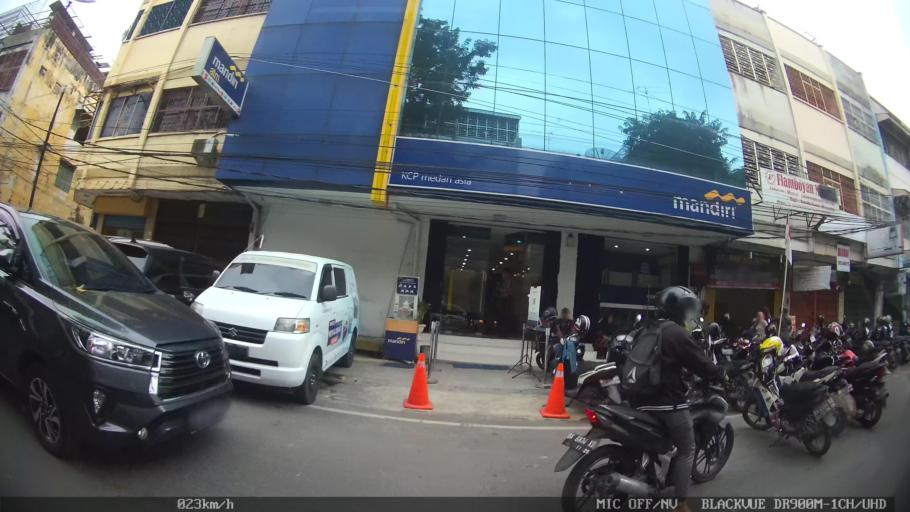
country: ID
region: North Sumatra
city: Medan
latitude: 3.5859
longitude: 98.6941
